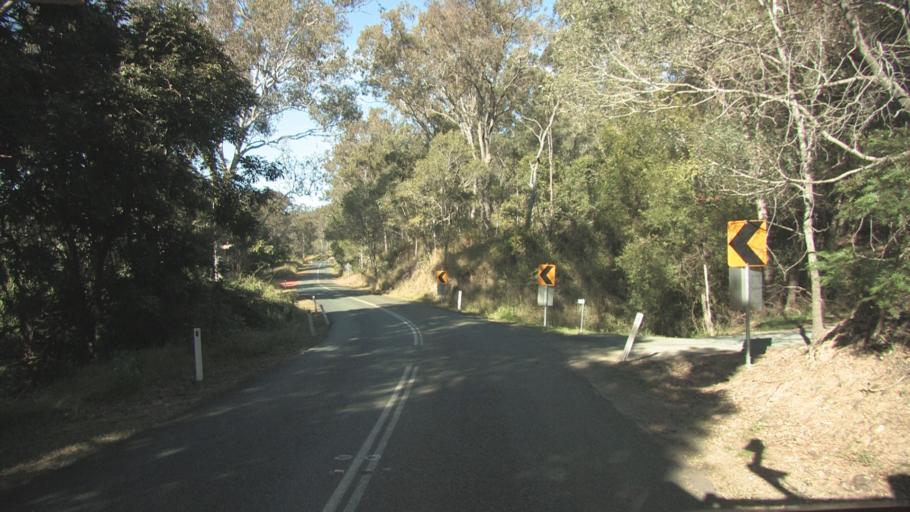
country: AU
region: Queensland
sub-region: Logan
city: Windaroo
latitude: -27.8013
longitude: 153.1684
